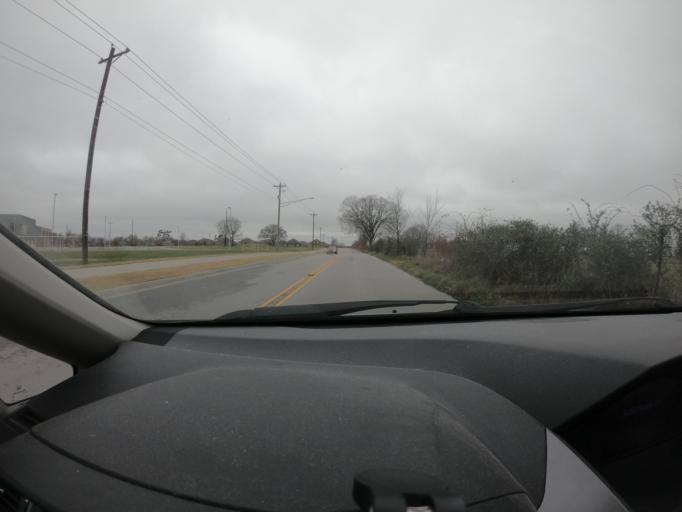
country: US
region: Arkansas
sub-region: Benton County
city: Bentonville
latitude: 36.3433
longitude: -94.2420
